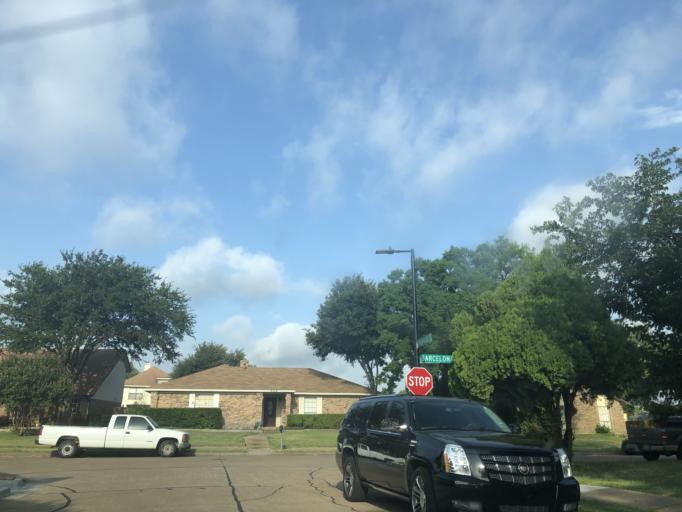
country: US
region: Texas
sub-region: Dallas County
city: Garland
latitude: 32.8549
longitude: -96.6315
